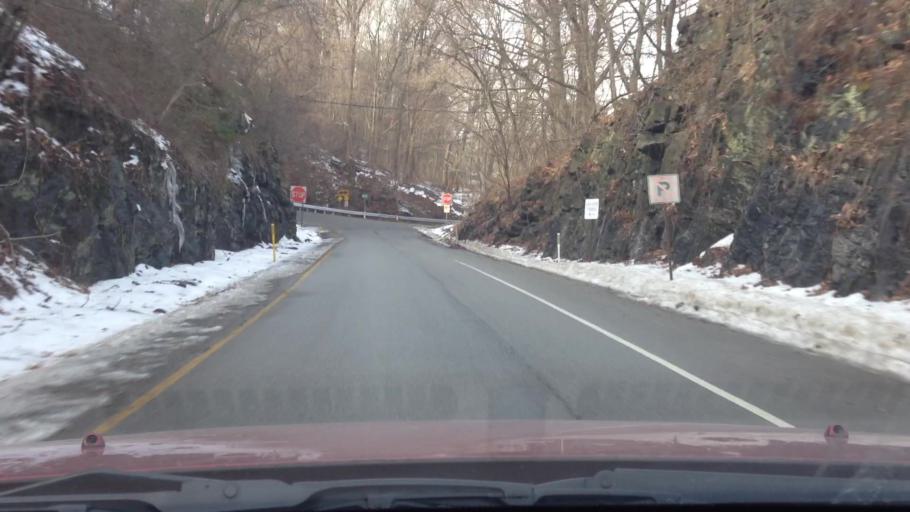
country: US
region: Pennsylvania
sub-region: Montgomery County
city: Narberth
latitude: 40.0408
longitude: -75.2502
